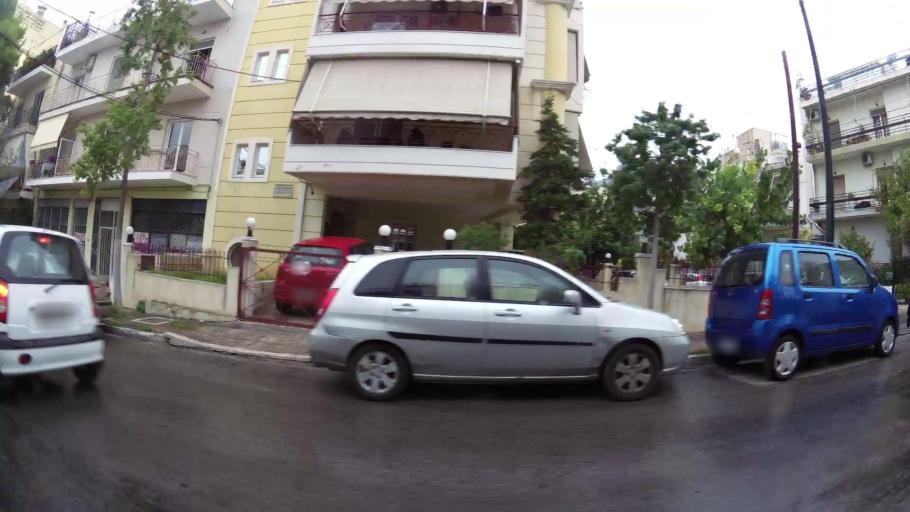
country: GR
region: Attica
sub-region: Nomarchia Athinas
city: Agia Varvara
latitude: 37.9896
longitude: 23.6532
